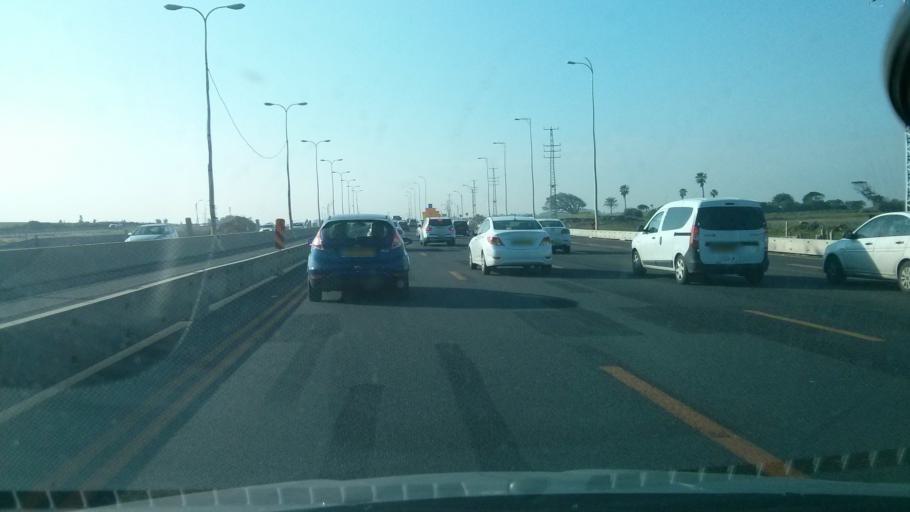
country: IL
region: Tel Aviv
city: Kefar Shemaryahu
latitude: 32.2379
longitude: 34.8331
